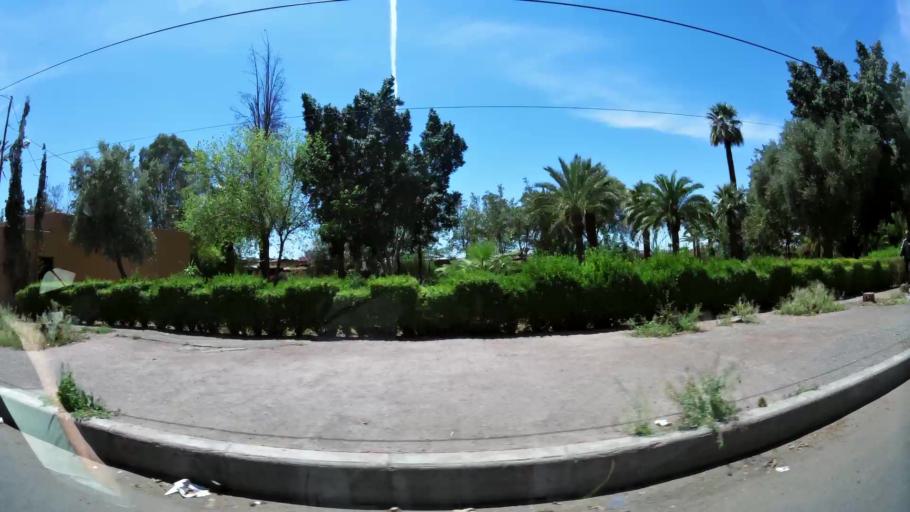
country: MA
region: Marrakech-Tensift-Al Haouz
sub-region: Marrakech
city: Marrakesh
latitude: 31.6322
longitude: -8.0417
